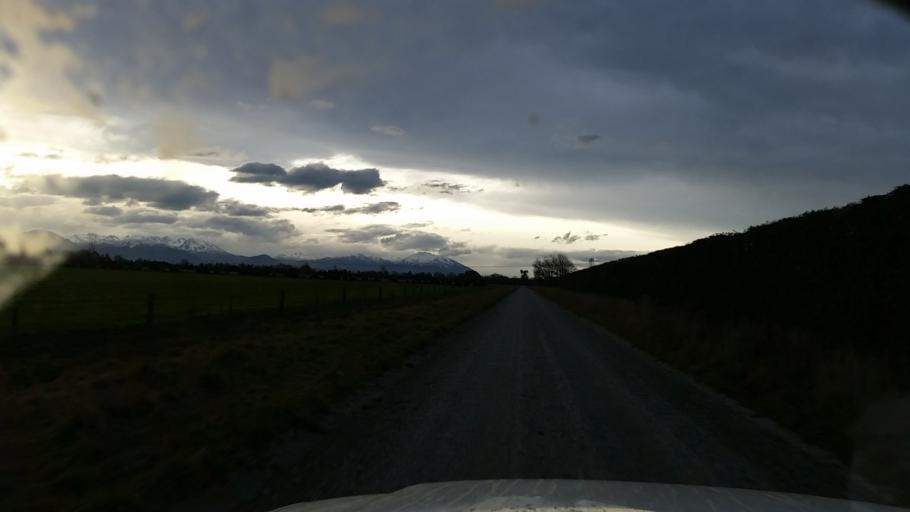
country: NZ
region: Canterbury
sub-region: Ashburton District
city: Ashburton
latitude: -43.8558
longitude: 171.6623
